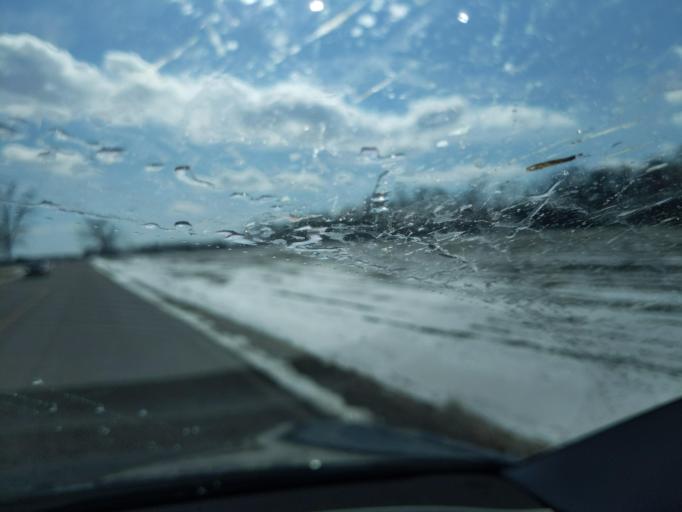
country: US
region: Michigan
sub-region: Livingston County
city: Fowlerville
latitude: 42.5975
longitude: -84.0894
